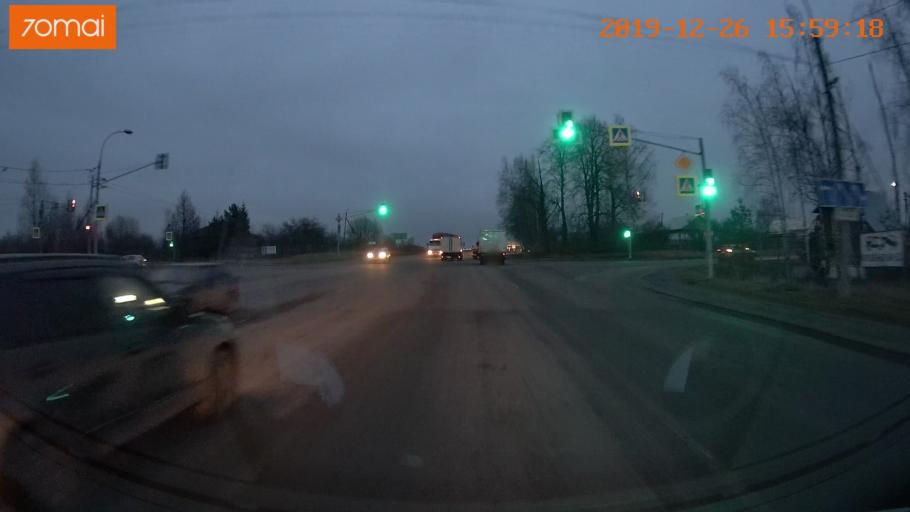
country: RU
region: Jaroslavl
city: Rybinsk
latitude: 58.0325
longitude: 38.8032
